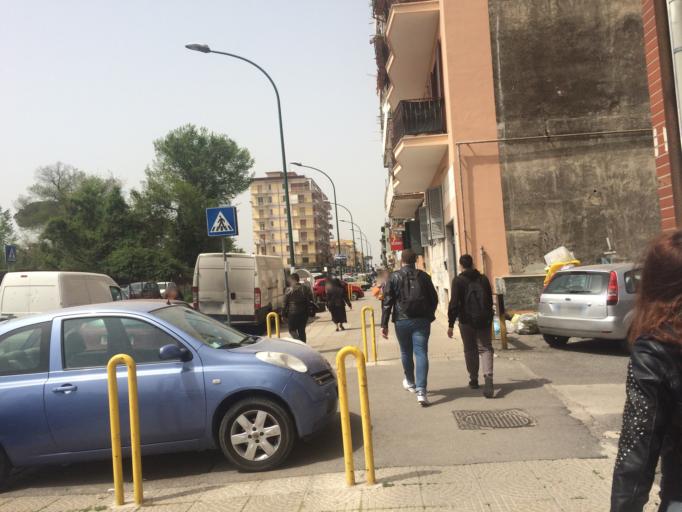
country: IT
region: Campania
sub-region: Provincia di Napoli
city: Mugnano di Napoli
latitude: 40.8910
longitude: 14.2222
